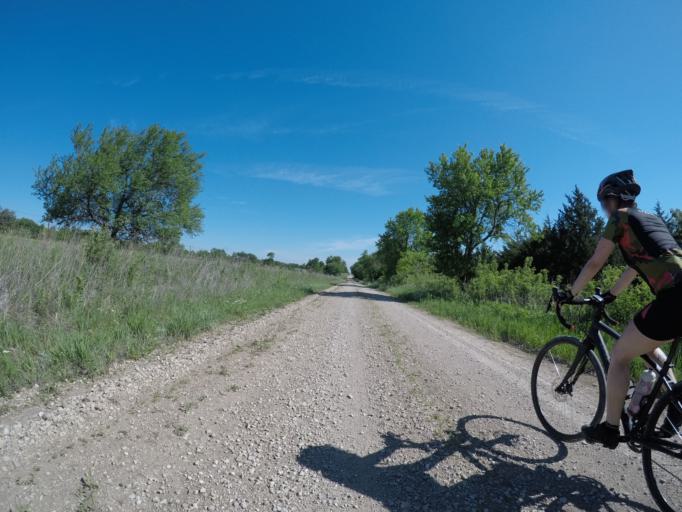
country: US
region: Kansas
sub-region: Wabaunsee County
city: Alma
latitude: 38.9374
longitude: -96.1138
